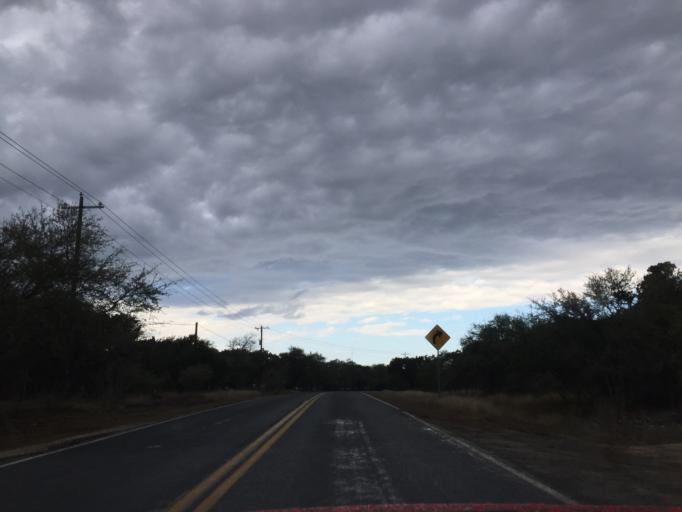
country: US
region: Texas
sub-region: Williamson County
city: Leander
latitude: 30.6095
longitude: -97.9354
